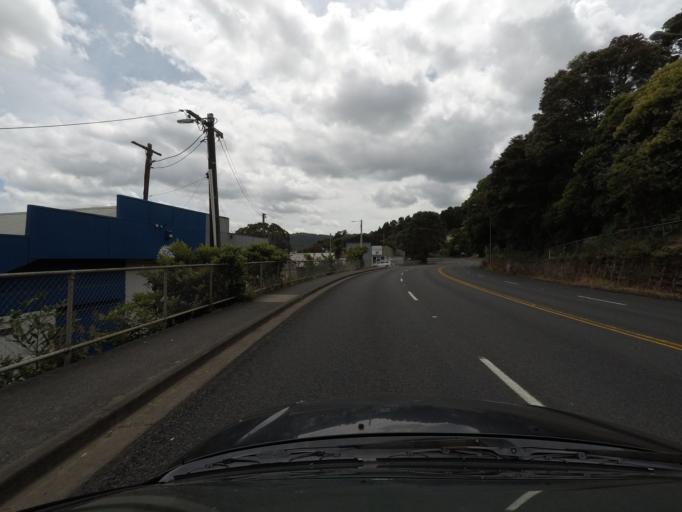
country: NZ
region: Northland
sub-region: Whangarei
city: Whangarei
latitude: -35.7263
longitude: 174.3322
